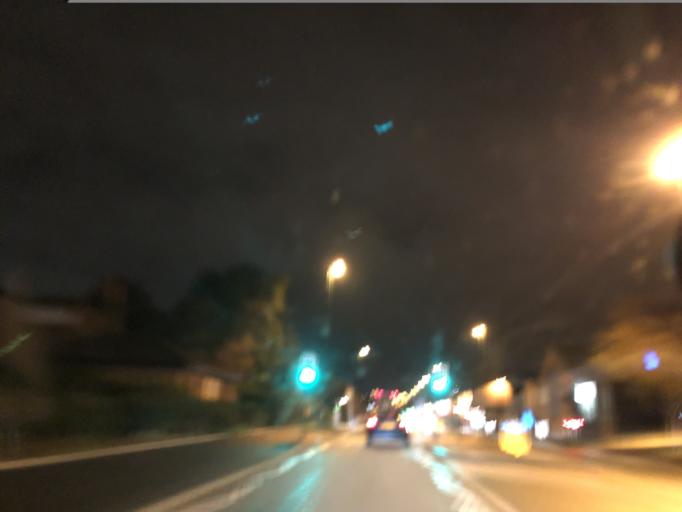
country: GB
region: England
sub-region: Manchester
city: Failsworth
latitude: 53.5131
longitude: -2.1535
